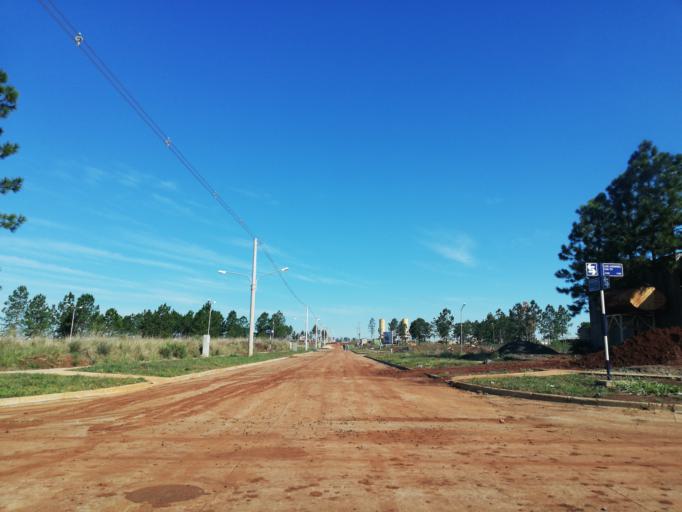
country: AR
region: Misiones
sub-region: Departamento de Capital
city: Posadas
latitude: -27.4038
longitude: -55.9916
